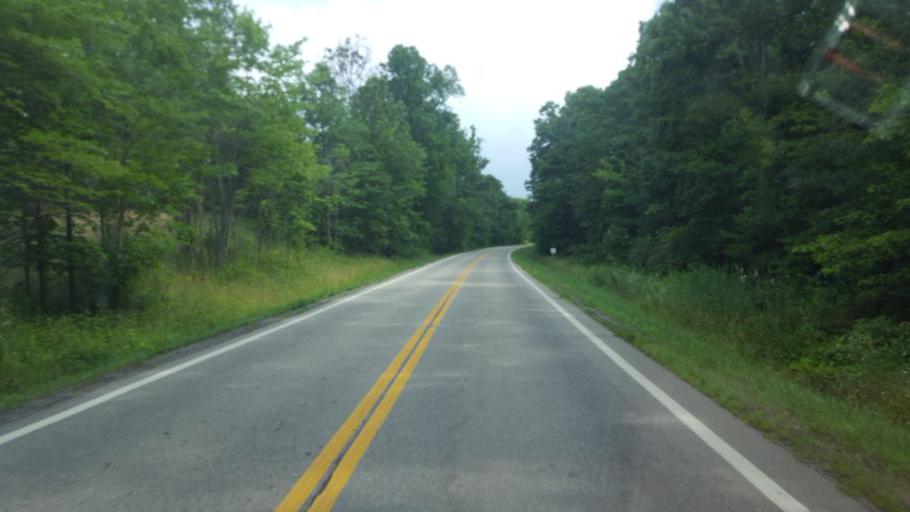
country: US
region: Ohio
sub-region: Columbiana County
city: Salineville
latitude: 40.6617
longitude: -80.8084
